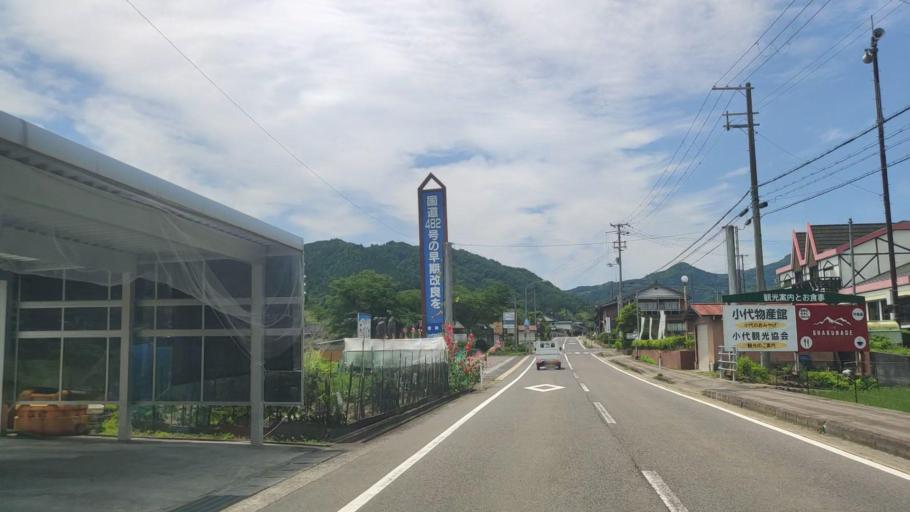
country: JP
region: Hyogo
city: Toyooka
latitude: 35.4686
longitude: 134.5487
